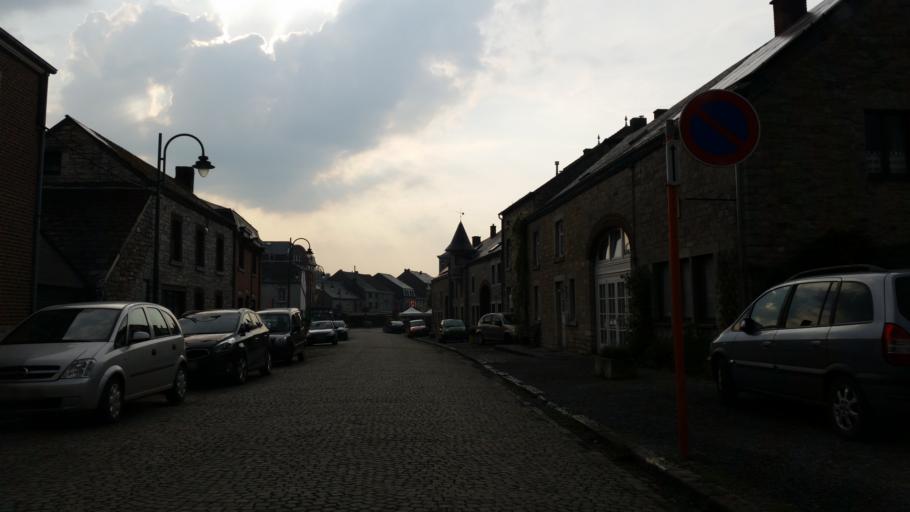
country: BE
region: Wallonia
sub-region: Province de Namur
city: Rochefort
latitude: 50.1247
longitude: 5.1907
